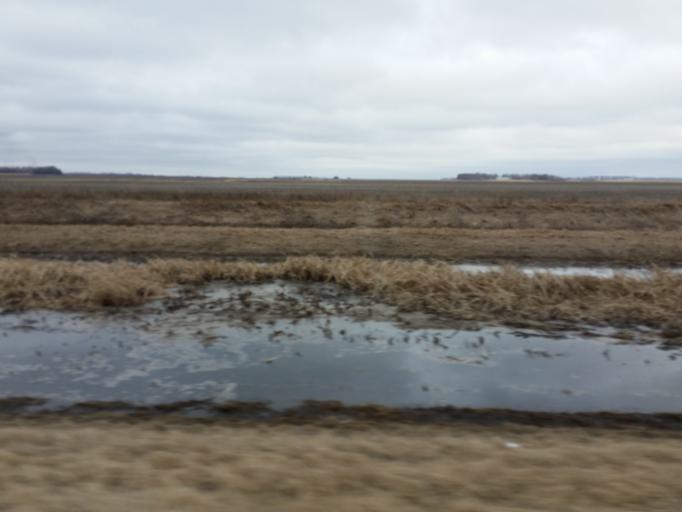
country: US
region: North Dakota
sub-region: Traill County
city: Hillsboro
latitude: 47.2256
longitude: -97.2176
